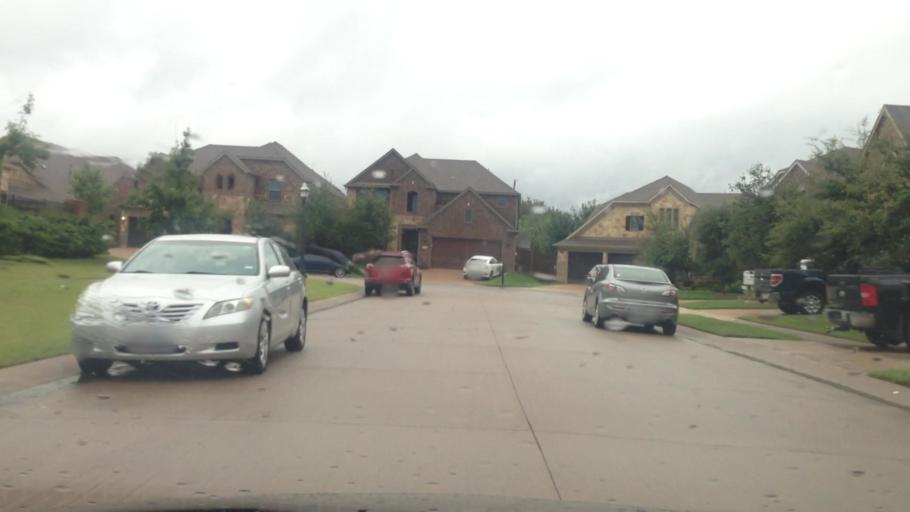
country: US
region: Texas
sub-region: Tarrant County
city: Colleyville
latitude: 32.8628
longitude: -97.1948
